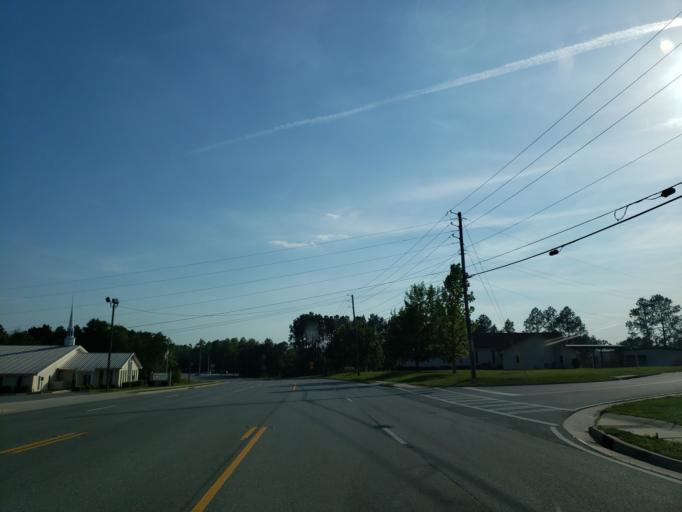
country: US
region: Georgia
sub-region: Tift County
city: Tifton
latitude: 31.4717
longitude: -83.5447
